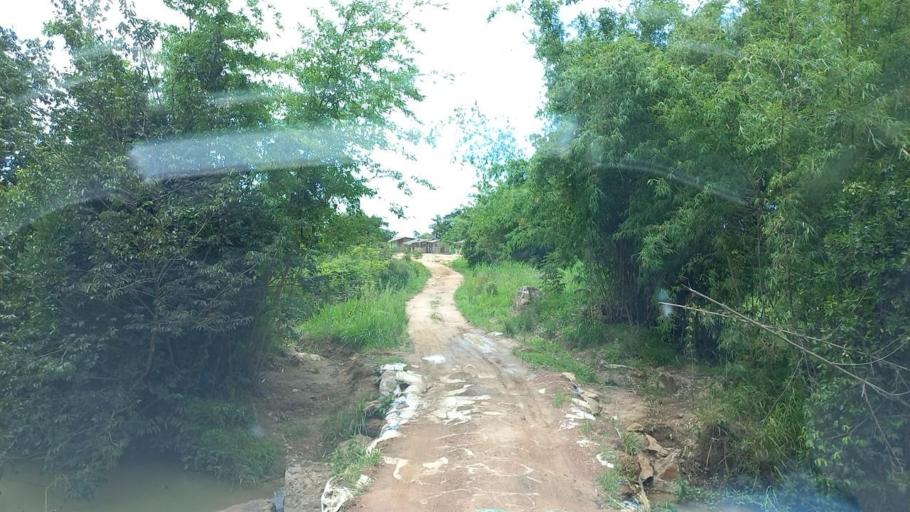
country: ZM
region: Copperbelt
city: Kitwe
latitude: -12.8184
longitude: 28.3884
